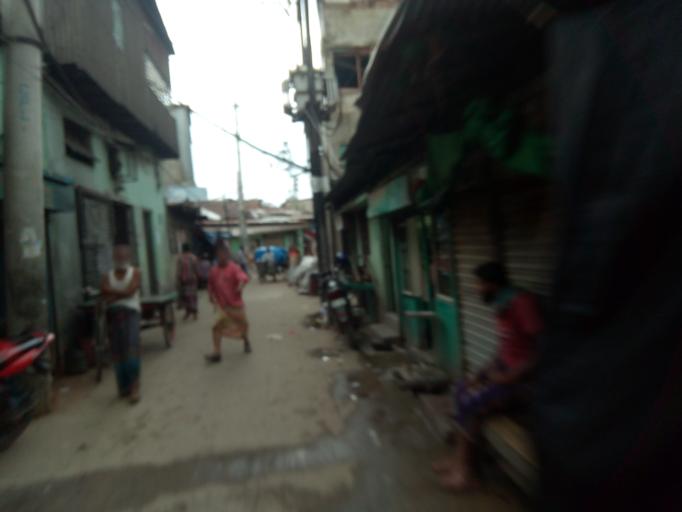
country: BD
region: Dhaka
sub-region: Dhaka
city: Dhaka
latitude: 23.7117
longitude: 90.3936
